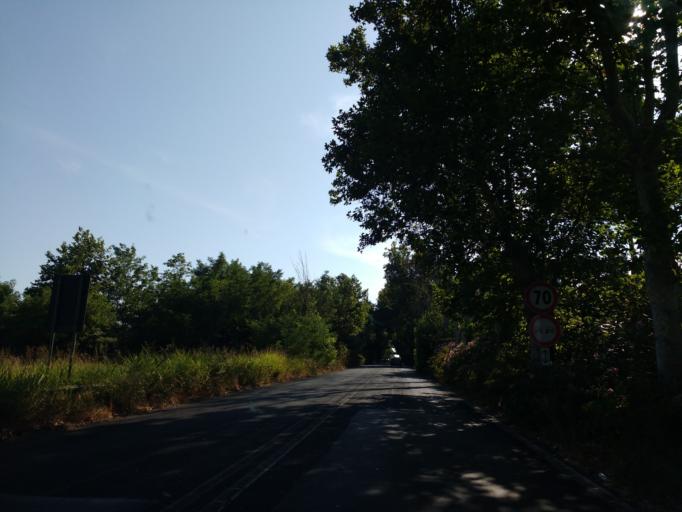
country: IT
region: Latium
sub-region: Citta metropolitana di Roma Capitale
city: Vitinia
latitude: 41.7887
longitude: 12.3735
